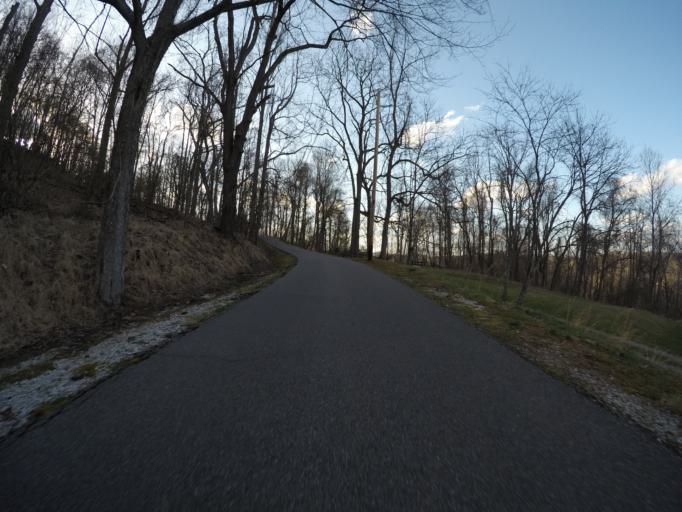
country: US
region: West Virginia
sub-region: Kanawha County
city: Charleston
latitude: 38.3904
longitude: -81.5644
